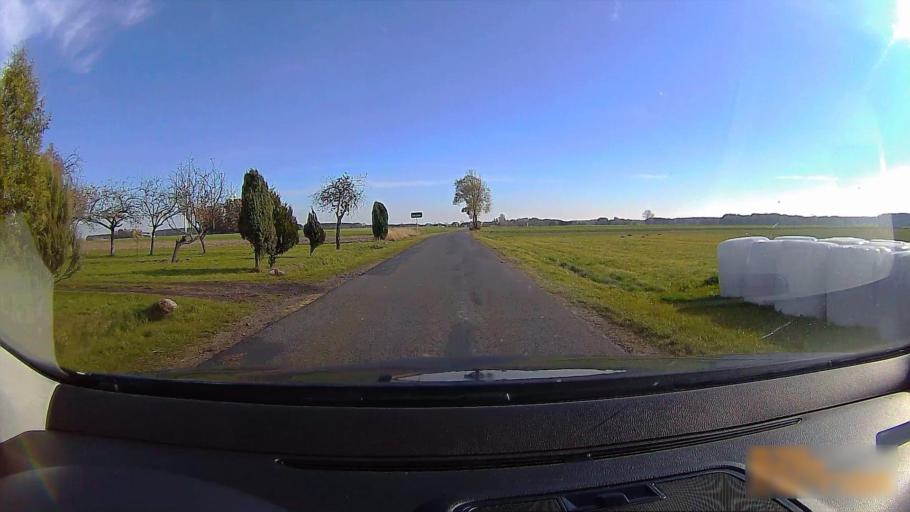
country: PL
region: Greater Poland Voivodeship
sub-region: Powiat ostrzeszowski
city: Doruchow
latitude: 51.3950
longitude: 18.0368
